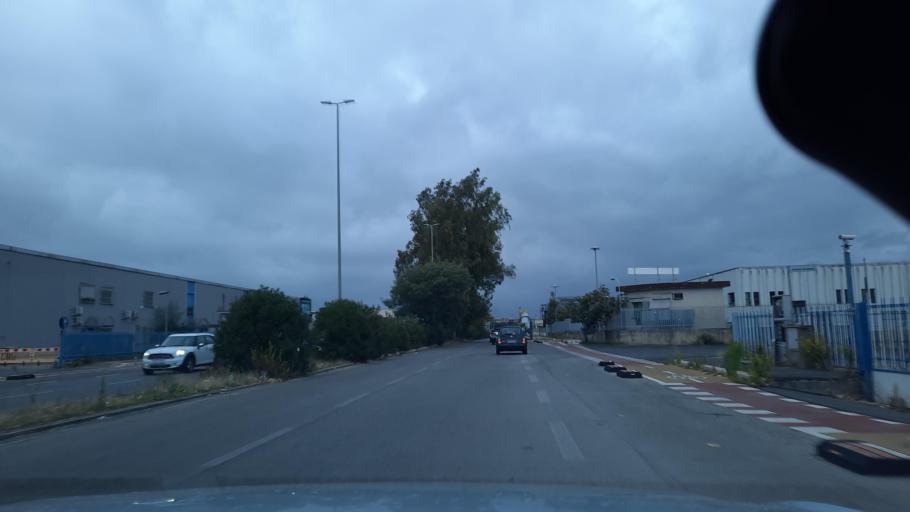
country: IT
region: Latium
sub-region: Citta metropolitana di Roma Capitale
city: Ciampino
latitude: 41.8453
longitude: 12.6105
